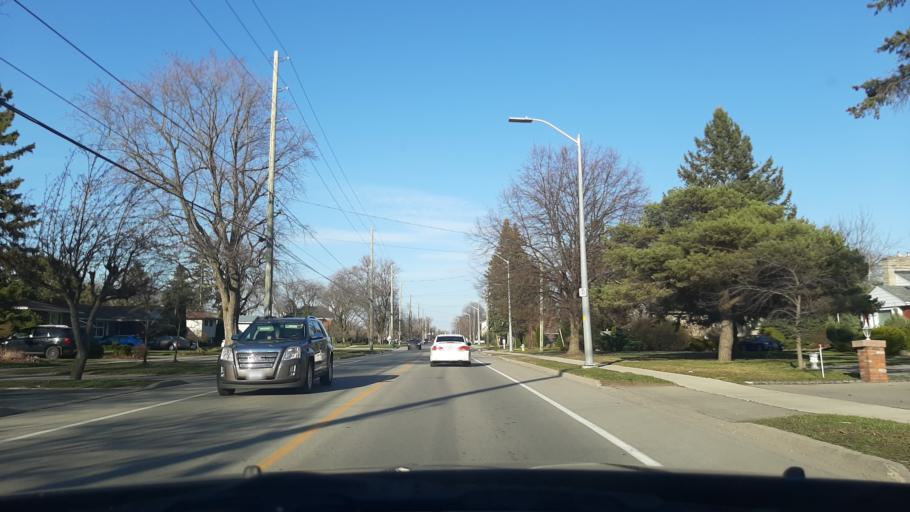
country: CA
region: Ontario
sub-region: Regional Municipality of Niagara
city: St. Catharines
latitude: 43.2075
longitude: -79.2367
